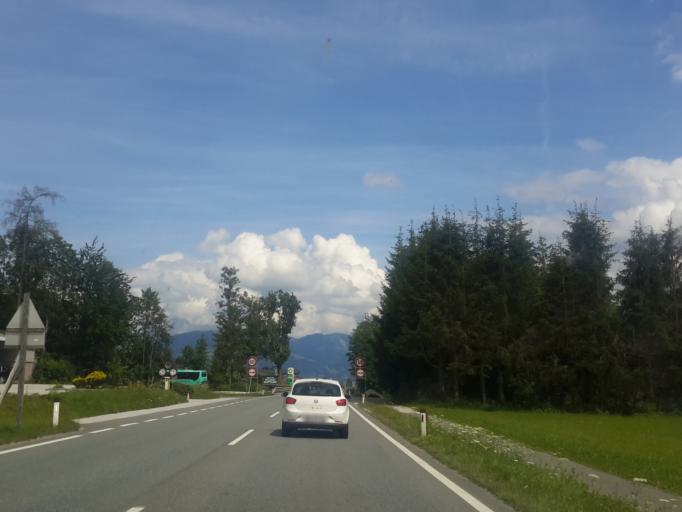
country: AT
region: Tyrol
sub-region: Politischer Bezirk Kufstein
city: Ellmau
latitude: 47.5156
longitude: 12.3144
